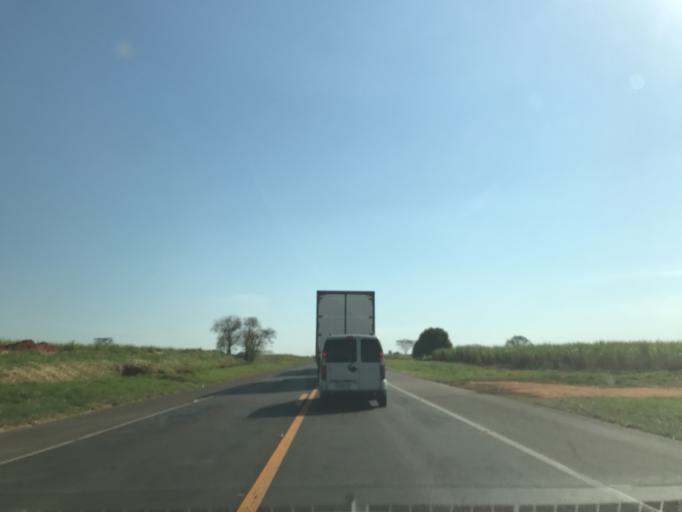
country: BR
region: Sao Paulo
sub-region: Penapolis
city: Penapolis
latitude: -21.4853
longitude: -50.2121
